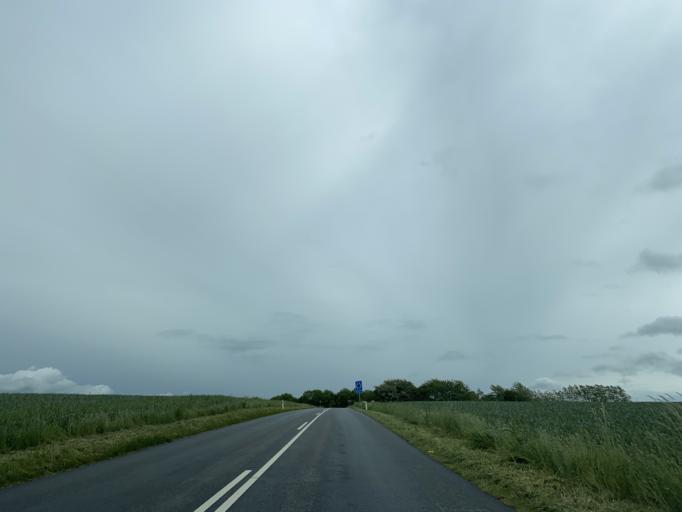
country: DK
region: Central Jutland
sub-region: Arhus Kommune
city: Sabro
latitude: 56.2504
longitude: 10.0117
